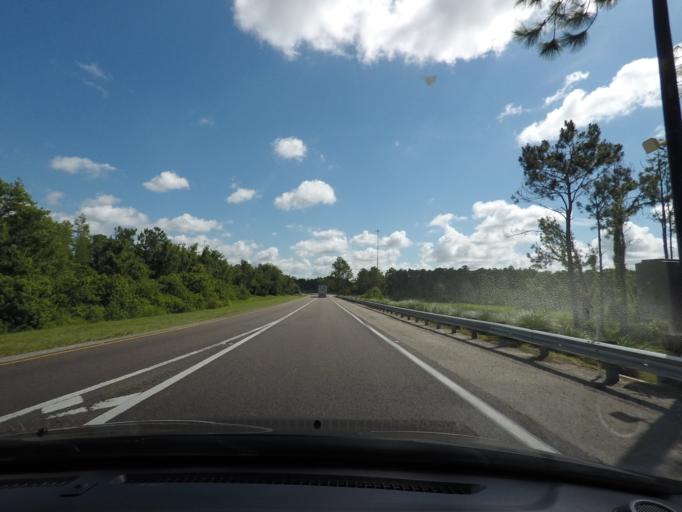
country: US
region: Florida
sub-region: Orange County
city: Conway
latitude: 28.4488
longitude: -81.2279
